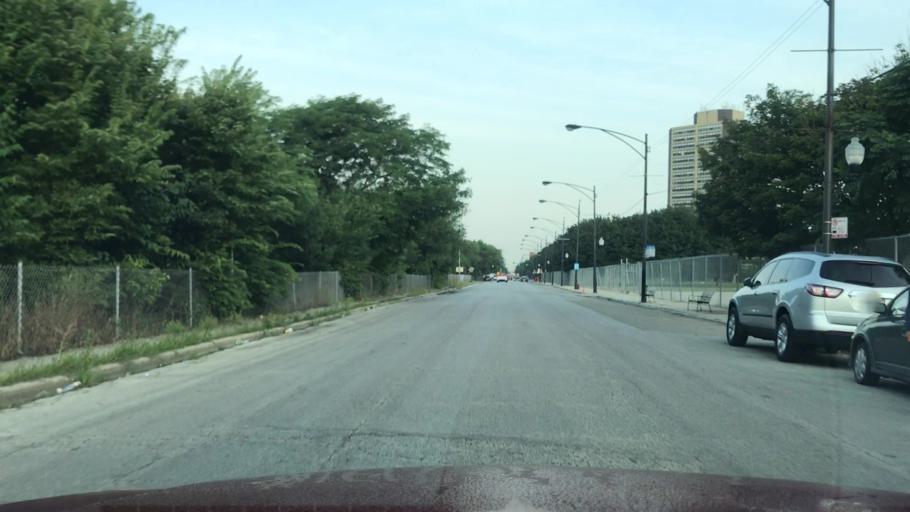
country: US
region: Illinois
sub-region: Cook County
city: Chicago
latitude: 41.8762
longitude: -87.6731
